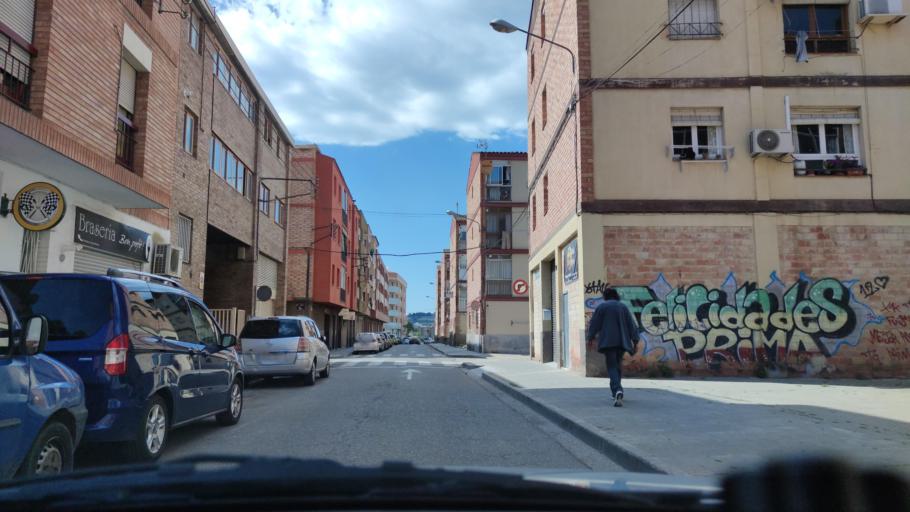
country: ES
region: Catalonia
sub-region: Provincia de Lleida
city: Lleida
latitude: 41.6059
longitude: 0.6449
